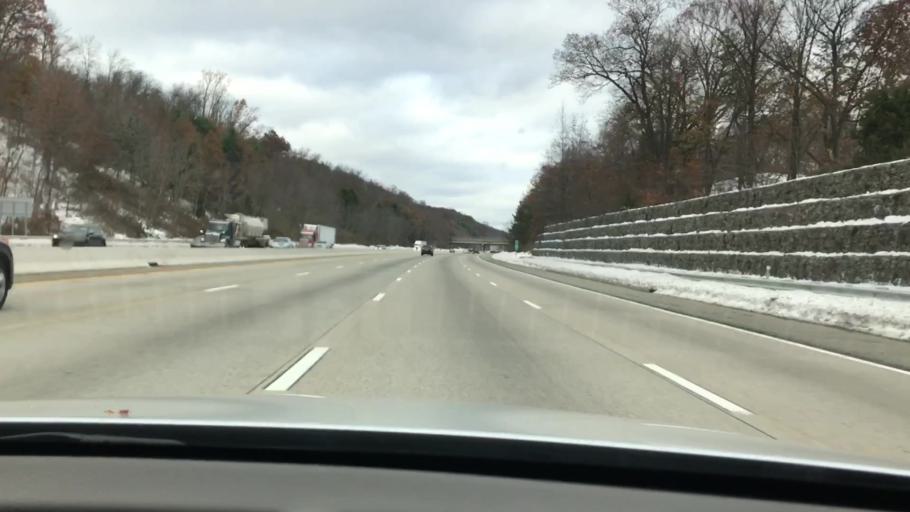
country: US
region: New Jersey
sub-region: Morris County
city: Lincoln Park
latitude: 40.9447
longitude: -74.3461
